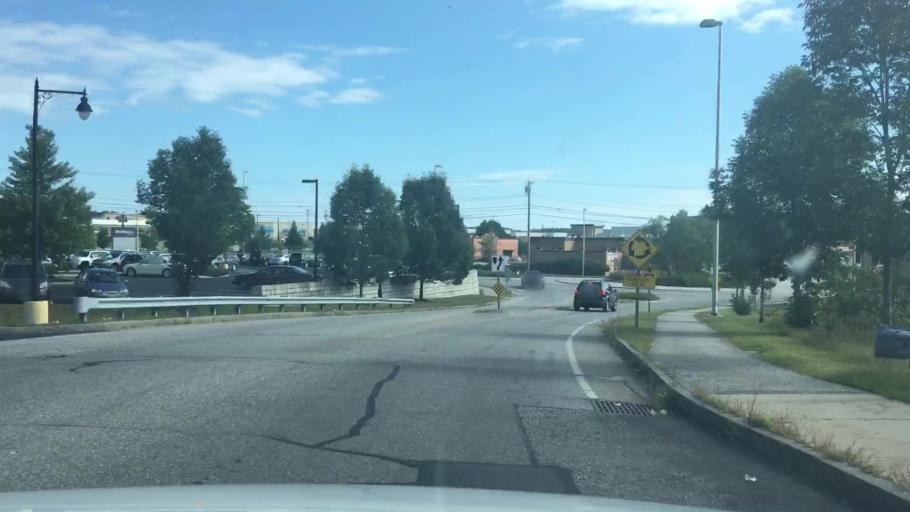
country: US
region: Maine
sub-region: Androscoggin County
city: Auburn
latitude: 44.1185
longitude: -70.2338
